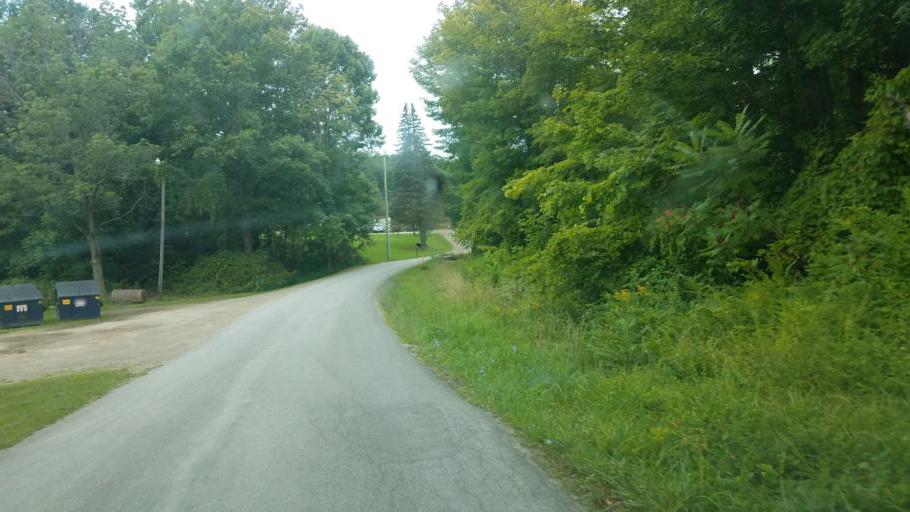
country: US
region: Pennsylvania
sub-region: Erie County
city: Lake City
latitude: 42.0014
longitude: -80.4374
